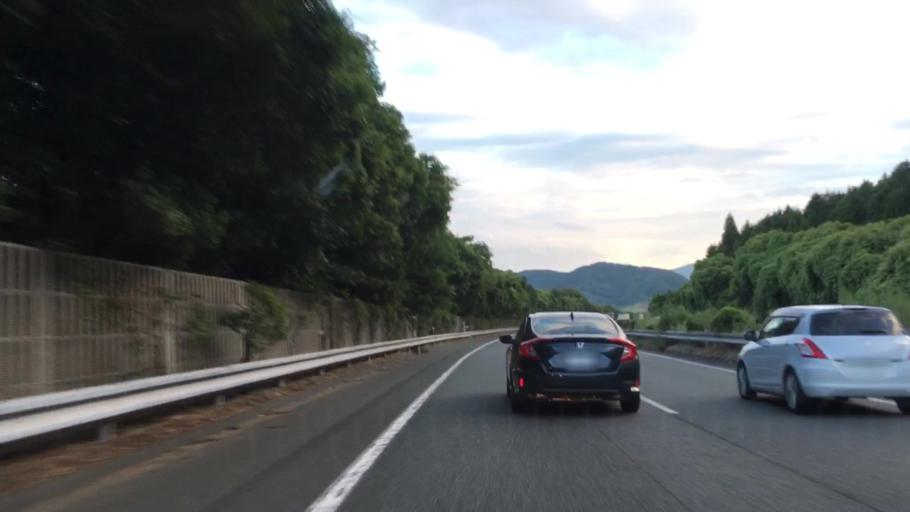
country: JP
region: Yamaguchi
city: Shimonoseki
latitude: 33.8787
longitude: 130.9701
